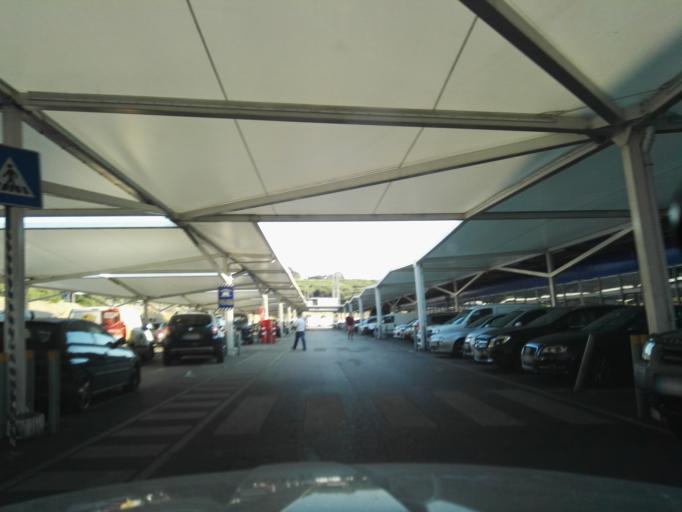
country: PT
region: Lisbon
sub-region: Oeiras
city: Alges
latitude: 38.7230
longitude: -9.2135
